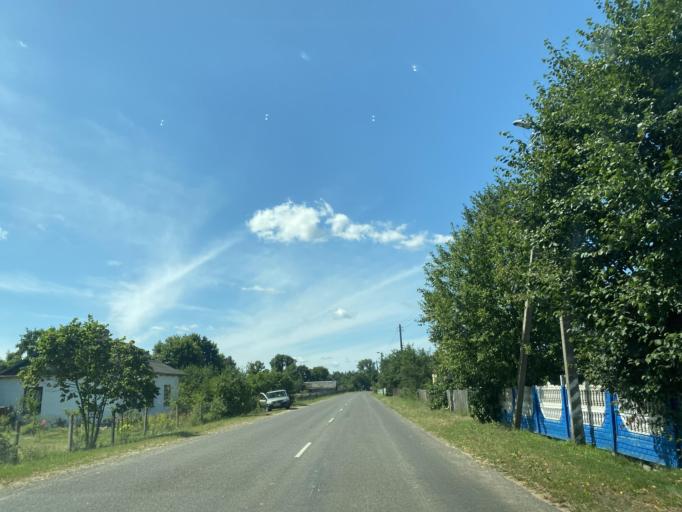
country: BY
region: Brest
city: Ivanava
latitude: 52.1831
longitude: 25.6065
